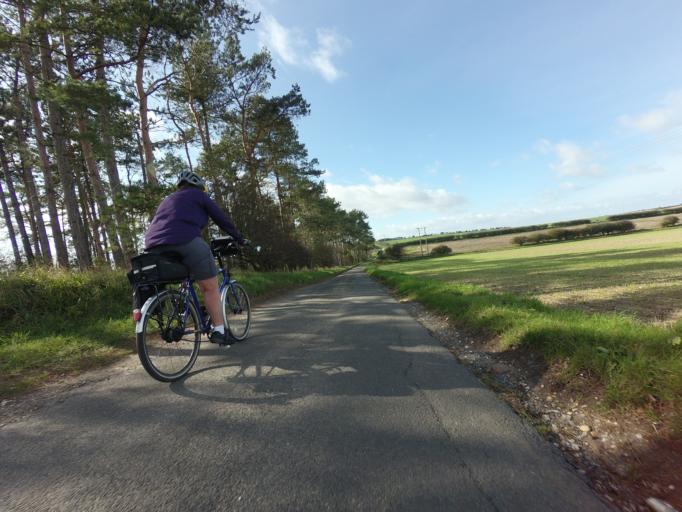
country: GB
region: England
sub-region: Norfolk
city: Hunstanton
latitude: 52.9363
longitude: 0.6286
